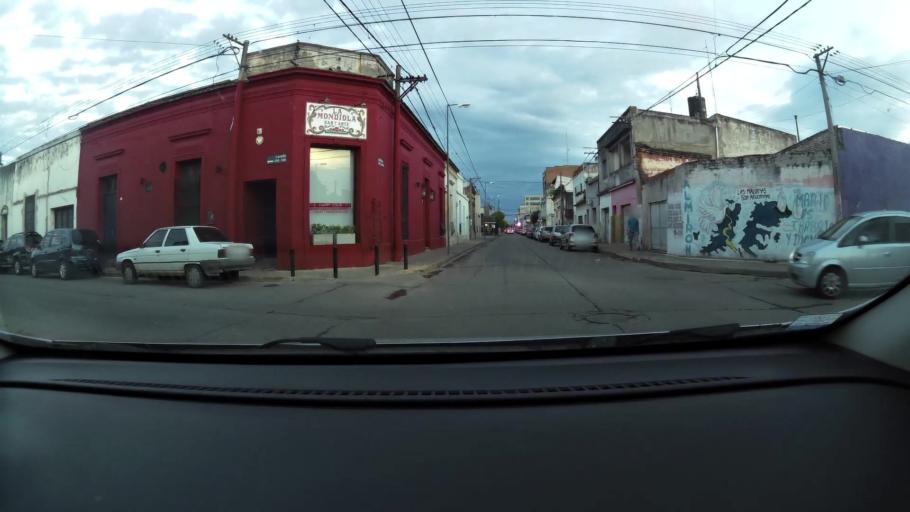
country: AR
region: Buenos Aires
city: San Nicolas de los Arroyos
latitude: -33.3308
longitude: -60.2230
